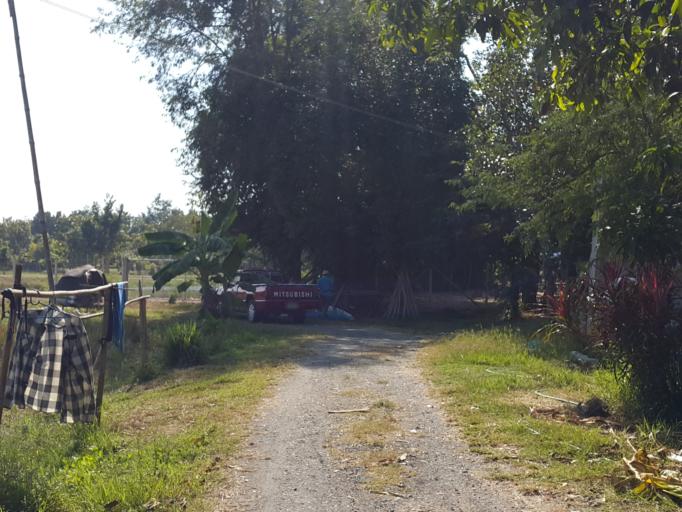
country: TH
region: Chiang Mai
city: San Kamphaeng
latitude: 18.8010
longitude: 99.0955
